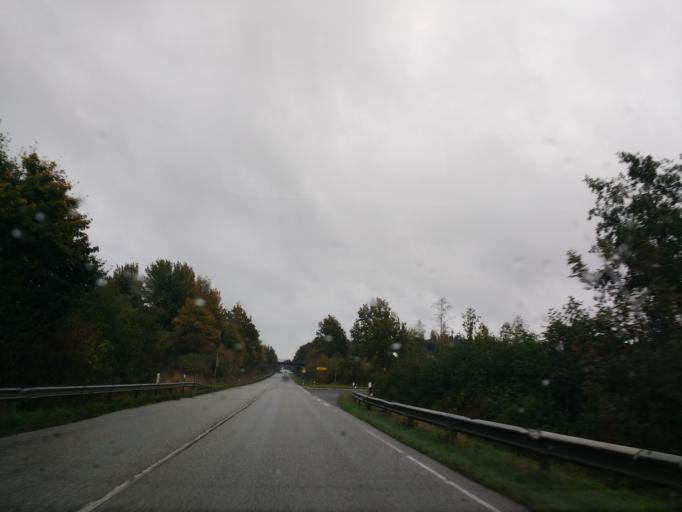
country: DE
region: Schleswig-Holstein
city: Susel
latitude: 54.0598
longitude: 10.7213
